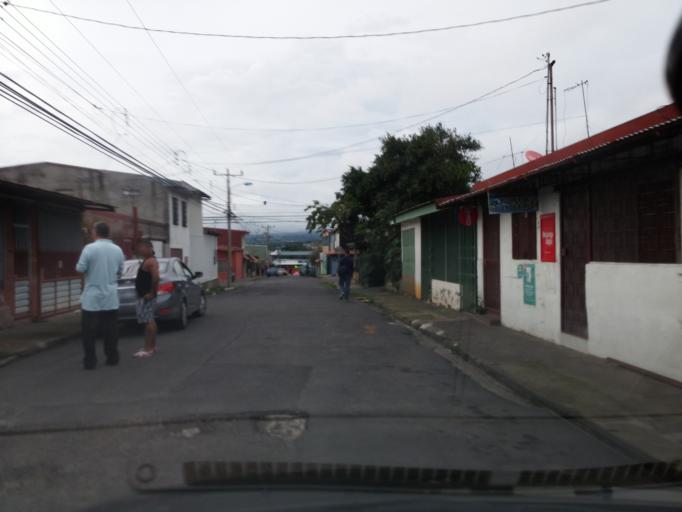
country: CR
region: Heredia
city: Heredia
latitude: 10.0103
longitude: -84.1174
